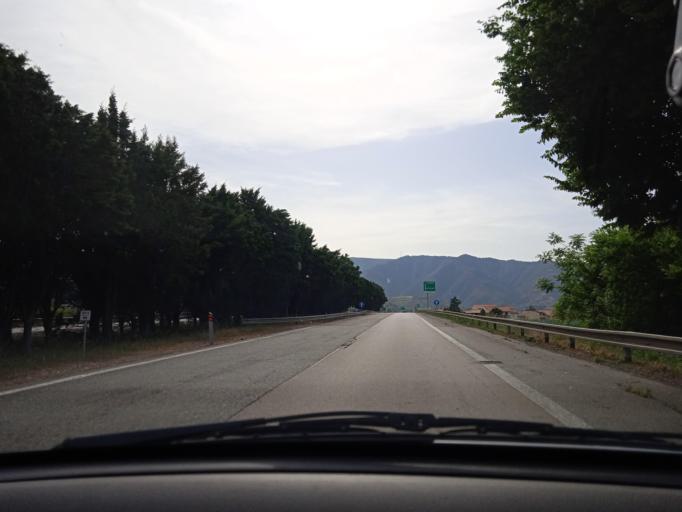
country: IT
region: Sicily
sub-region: Messina
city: Falcone
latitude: 38.1139
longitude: 15.0881
